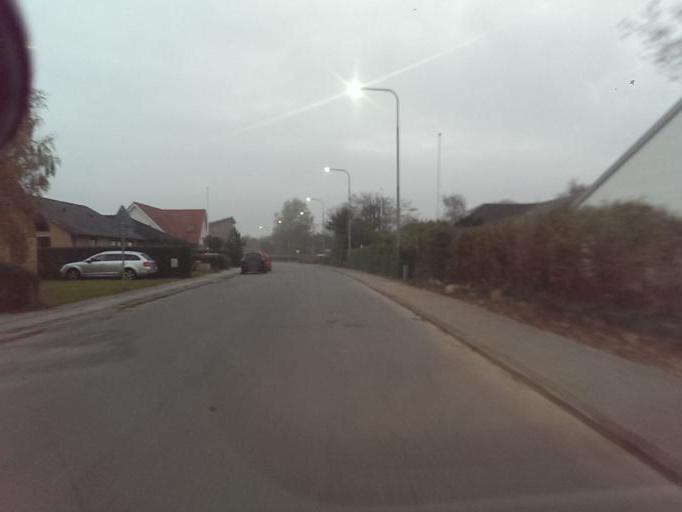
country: DK
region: South Denmark
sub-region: Esbjerg Kommune
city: Esbjerg
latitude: 55.5058
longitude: 8.4455
